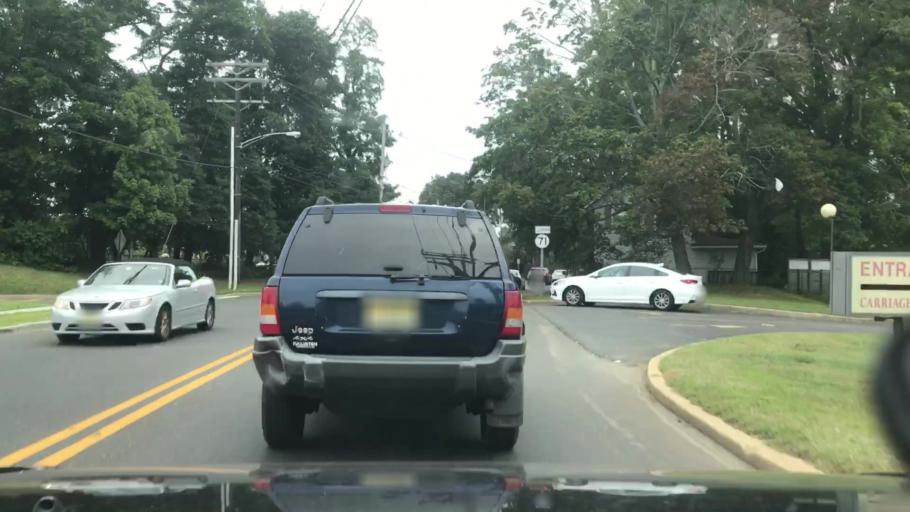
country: US
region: New Jersey
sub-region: Monmouth County
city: West Long Branch
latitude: 40.2946
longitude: -74.0280
